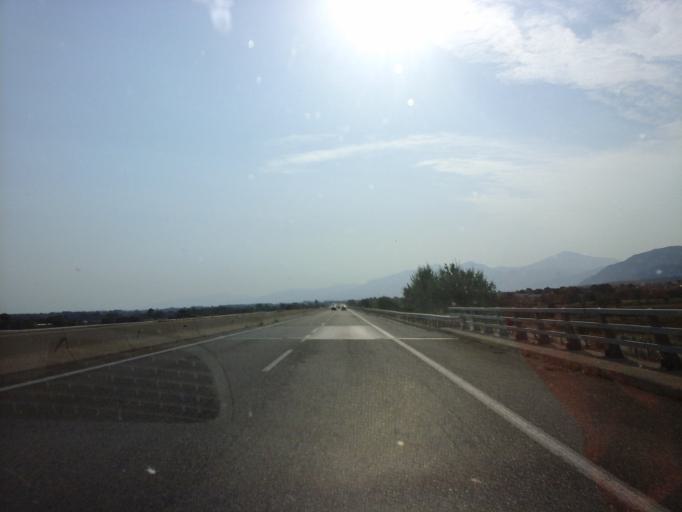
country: GR
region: East Macedonia and Thrace
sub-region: Nomos Xanthis
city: Selero
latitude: 41.1201
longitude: 25.0608
